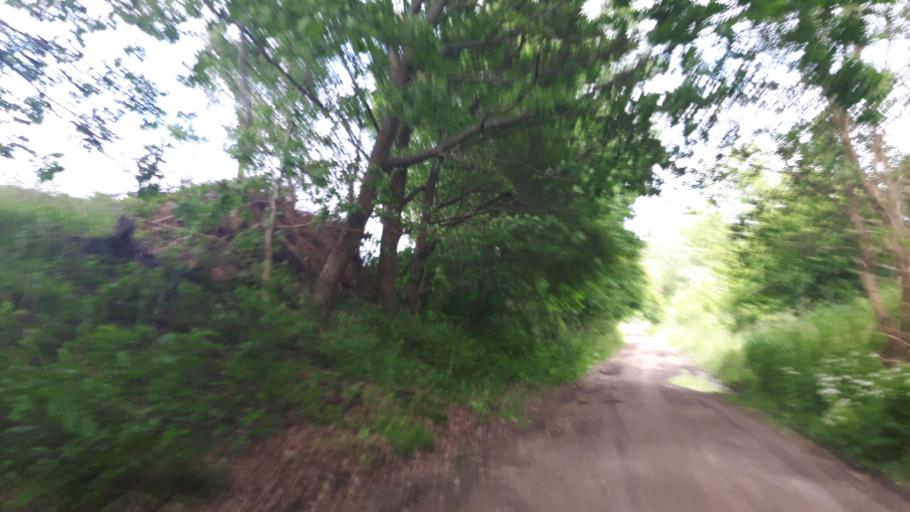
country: PL
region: Pomeranian Voivodeship
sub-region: Powiat slupski
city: Ustka
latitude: 54.5912
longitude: 16.9659
